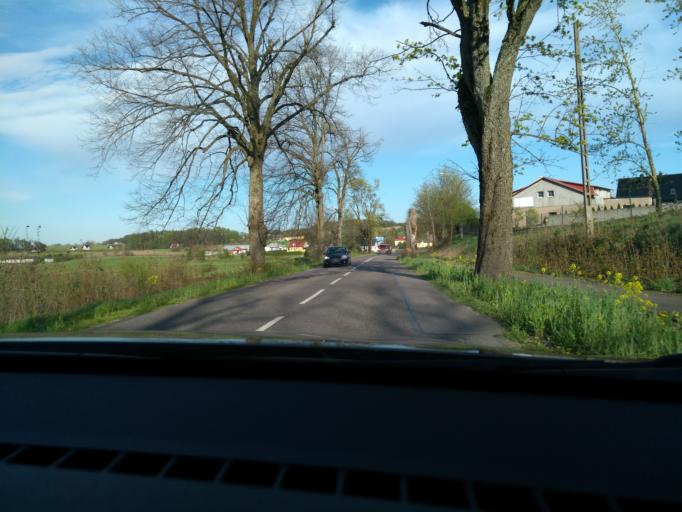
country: PL
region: Pomeranian Voivodeship
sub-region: Powiat kartuski
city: Suleczyno
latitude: 54.3272
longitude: 17.7862
